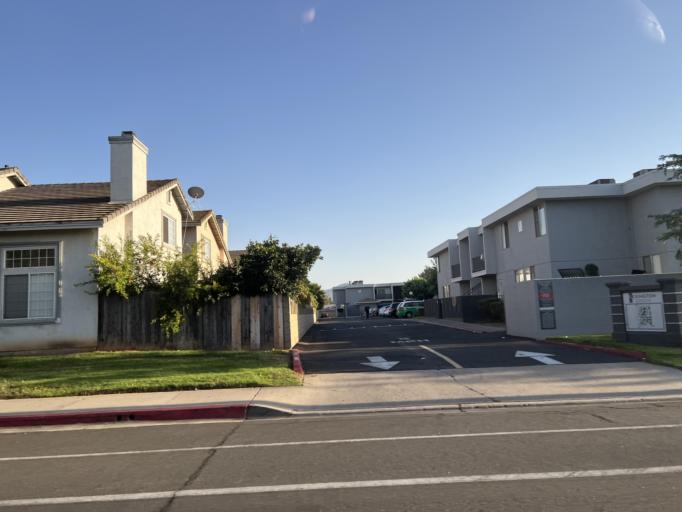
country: US
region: California
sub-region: San Diego County
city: Bostonia
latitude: 32.7928
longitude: -116.9293
